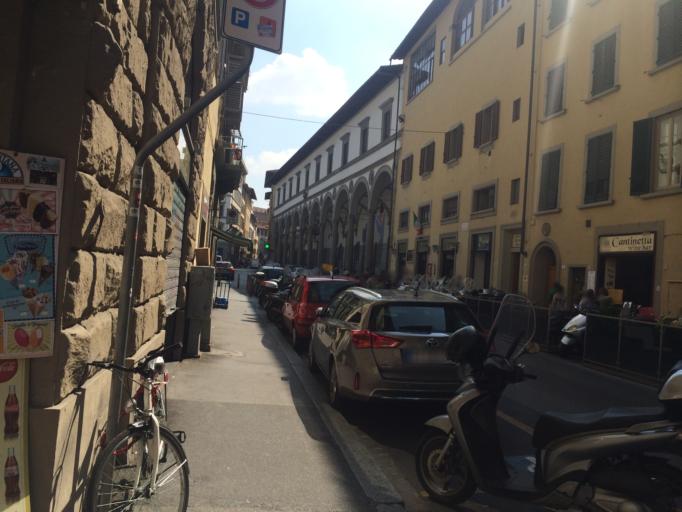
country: IT
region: Tuscany
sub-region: Province of Florence
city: Florence
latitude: 43.7735
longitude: 11.2486
